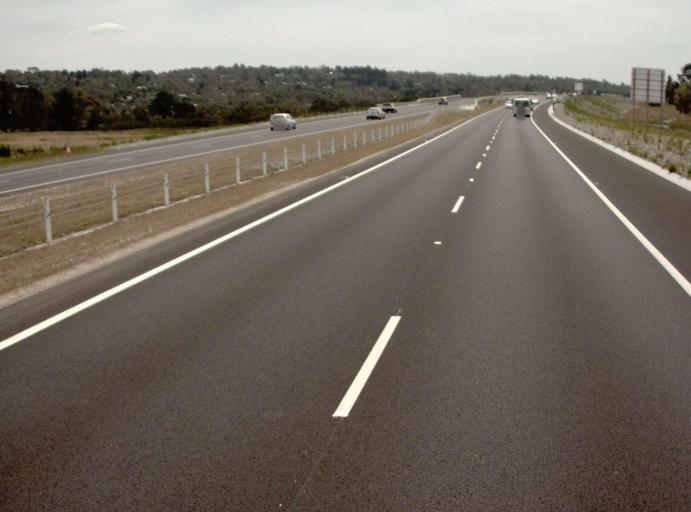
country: AU
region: Victoria
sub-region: Mornington Peninsula
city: Moorooduc
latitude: -38.2128
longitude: 145.1302
